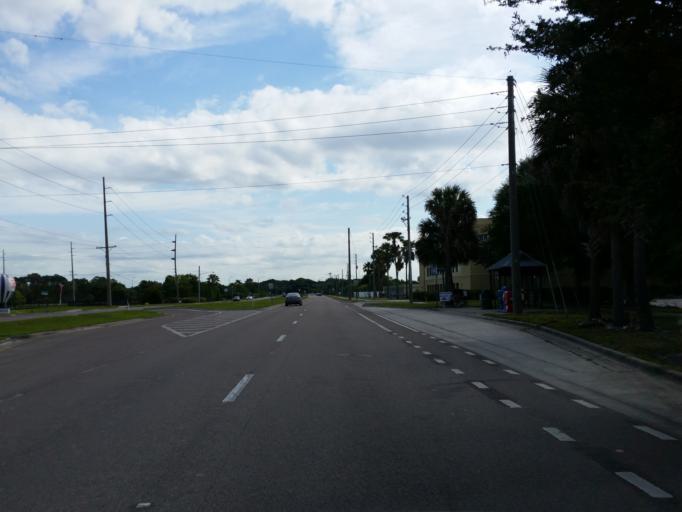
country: US
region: Florida
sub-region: Hillsborough County
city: Brandon
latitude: 27.9255
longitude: -82.3156
